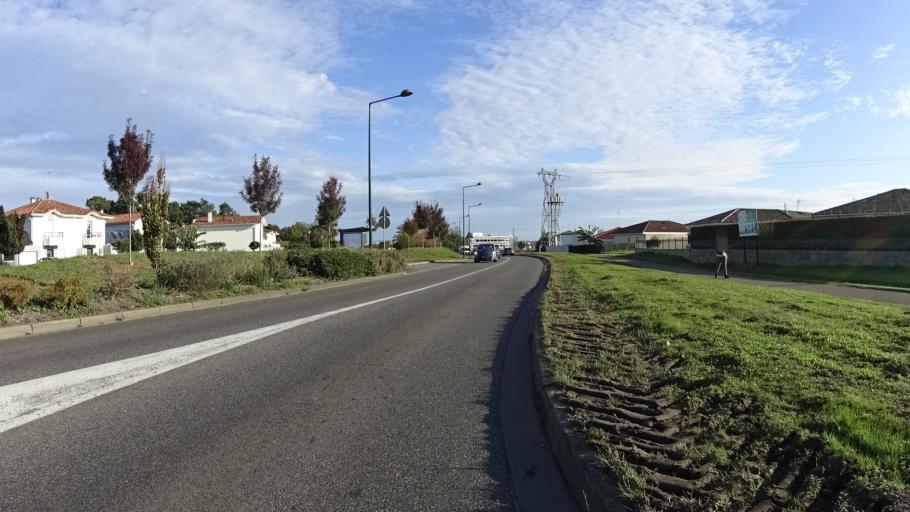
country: FR
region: Aquitaine
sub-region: Departement des Landes
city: Saint-Paul-les-Dax
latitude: 43.7346
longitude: -1.0475
